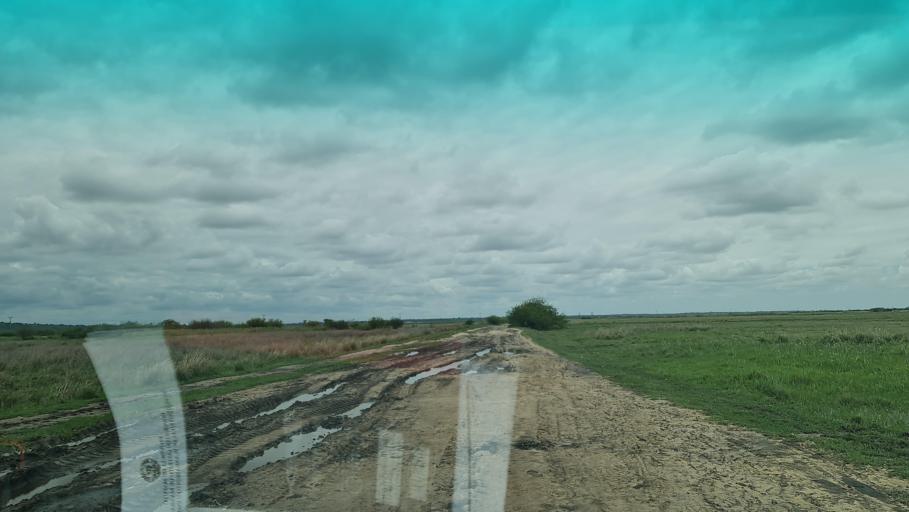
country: MZ
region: Maputo City
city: Maputo
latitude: -25.7292
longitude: 32.7037
